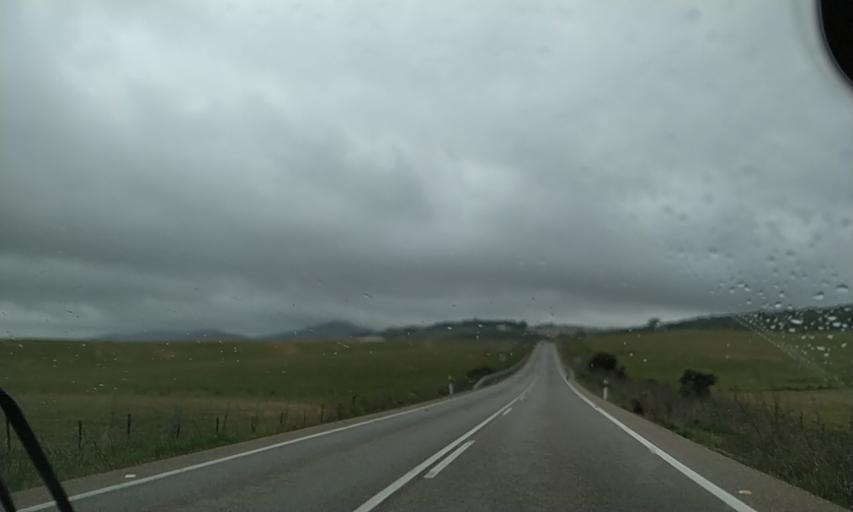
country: ES
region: Extremadura
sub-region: Provincia de Caceres
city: Caceres
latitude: 39.4981
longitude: -6.3874
